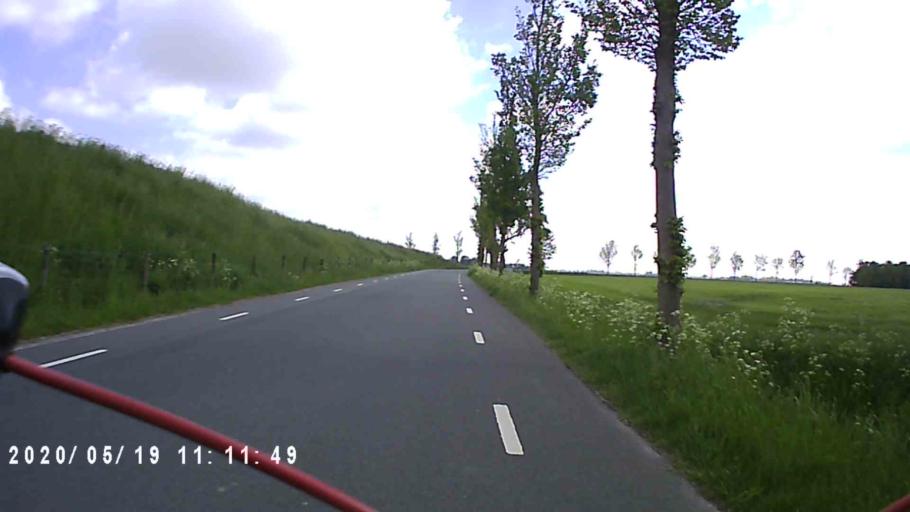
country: NL
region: Groningen
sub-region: Gemeente Zuidhorn
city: Grijpskerk
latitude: 53.2890
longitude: 6.3317
